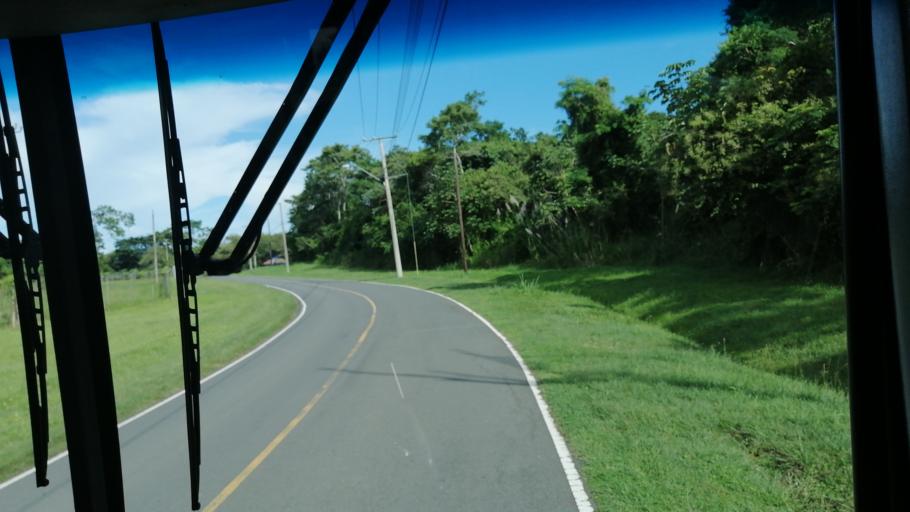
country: PA
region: Panama
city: Veracruz
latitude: 8.9010
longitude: -79.5855
